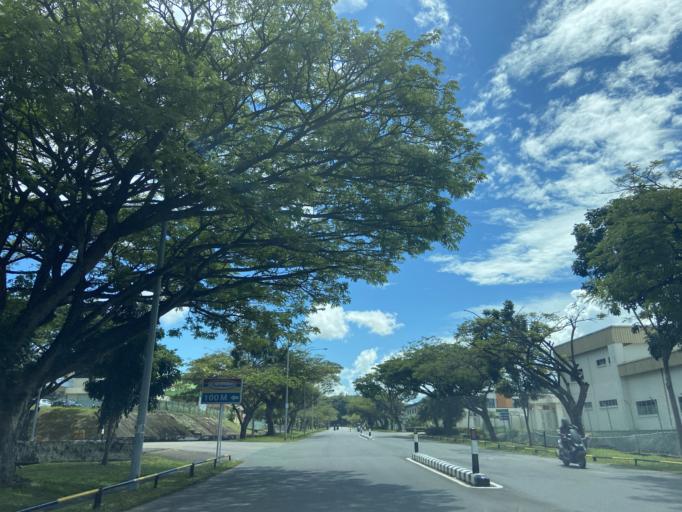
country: SG
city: Singapore
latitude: 1.0595
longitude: 104.0342
